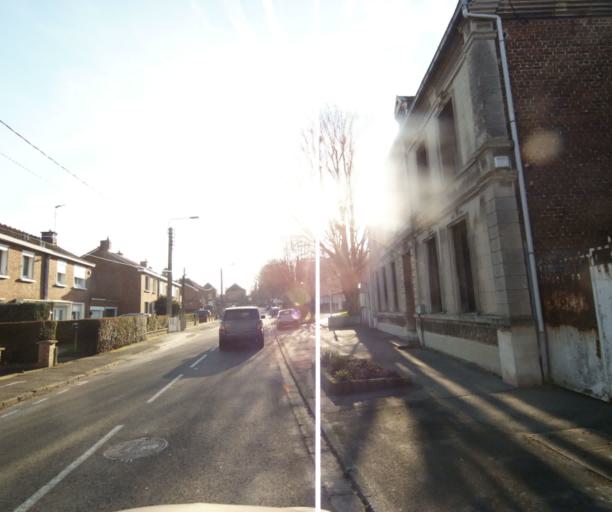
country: FR
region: Nord-Pas-de-Calais
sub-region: Departement du Nord
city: Saultain
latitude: 50.3375
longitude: 3.5771
